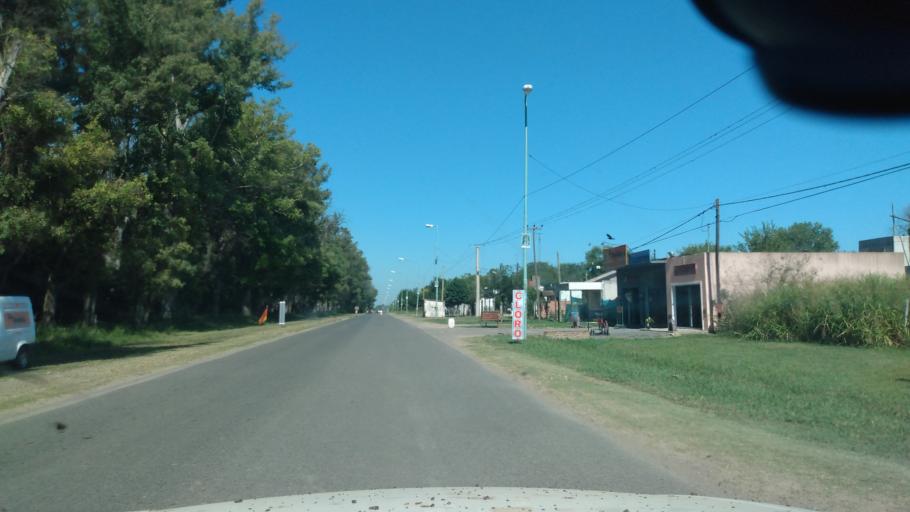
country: AR
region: Buenos Aires
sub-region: Partido de Lujan
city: Lujan
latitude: -34.5031
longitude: -59.0734
